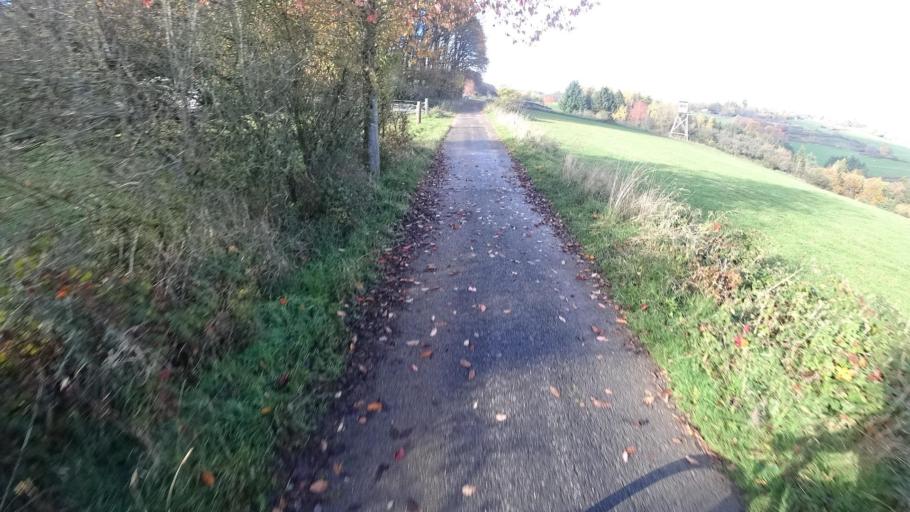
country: DE
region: Rheinland-Pfalz
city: Lind
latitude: 50.4854
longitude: 6.9424
